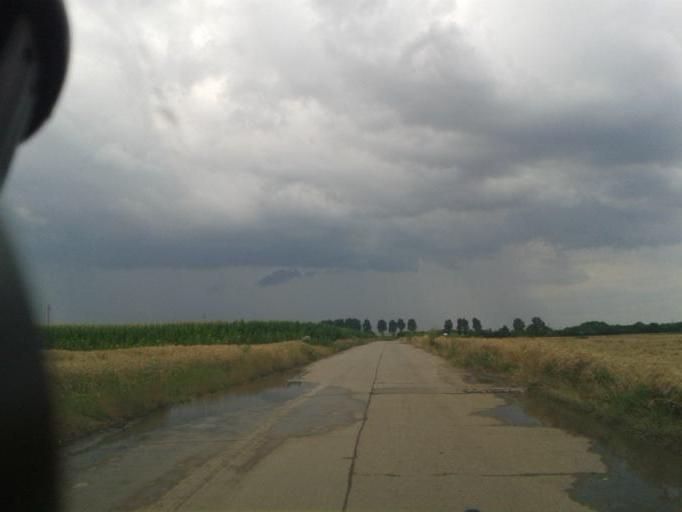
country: RO
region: Calarasi
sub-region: Comuna Belciugatele
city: Belciugatele
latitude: 44.5223
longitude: 26.4840
